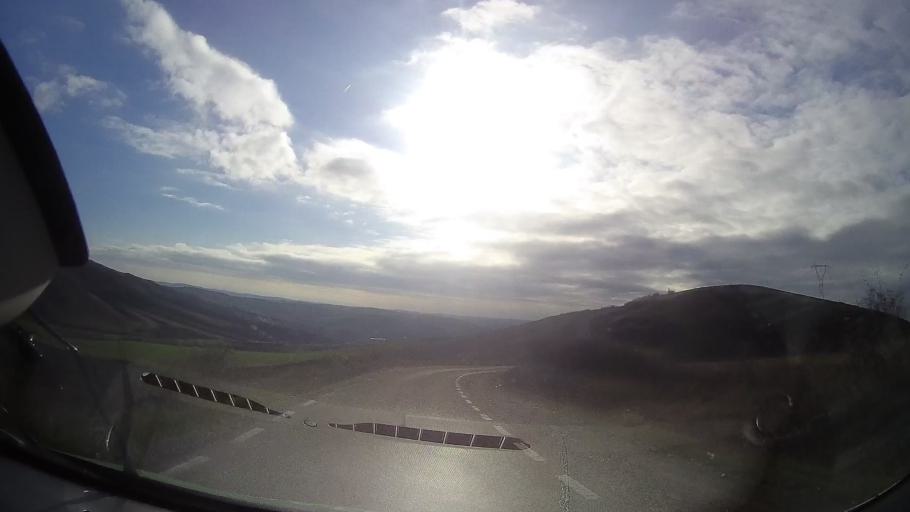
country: RO
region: Mures
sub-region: Comuna Sanger
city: Sanger
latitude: 46.5535
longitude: 24.1610
